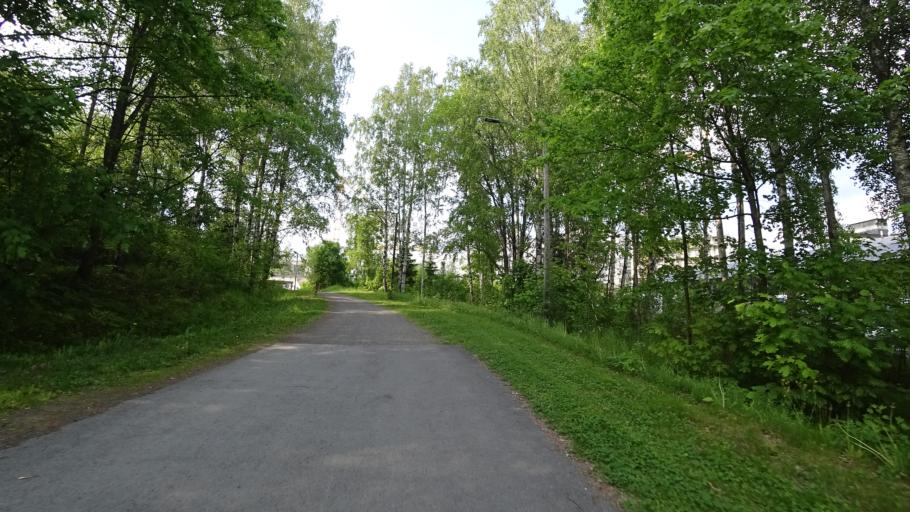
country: FI
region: Pirkanmaa
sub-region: Tampere
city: Pirkkala
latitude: 61.5027
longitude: 23.6305
